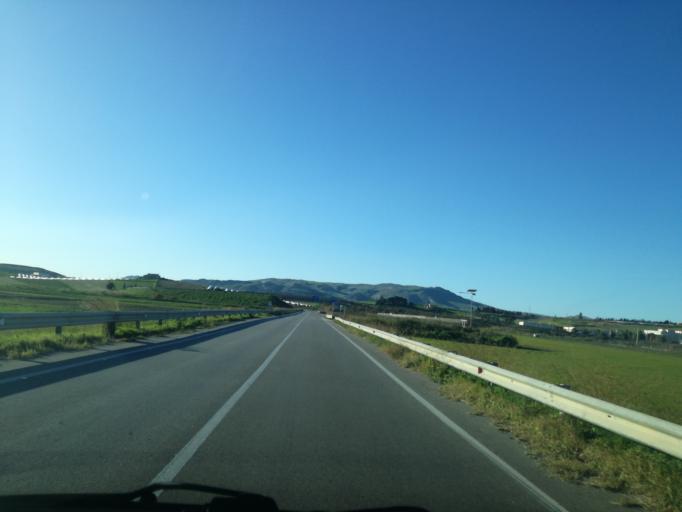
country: IT
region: Sicily
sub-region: Provincia di Caltanissetta
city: Butera
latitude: 37.1247
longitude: 14.1225
